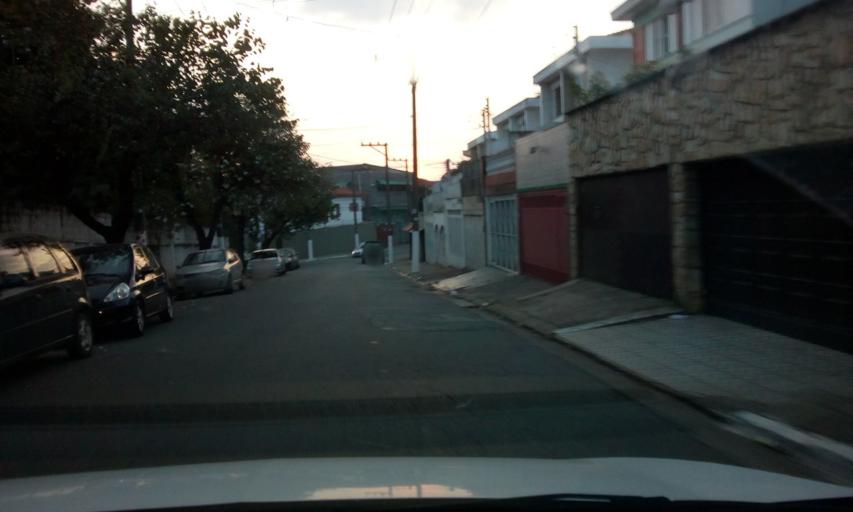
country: BR
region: Sao Paulo
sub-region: Diadema
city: Diadema
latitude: -23.6400
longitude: -46.6584
